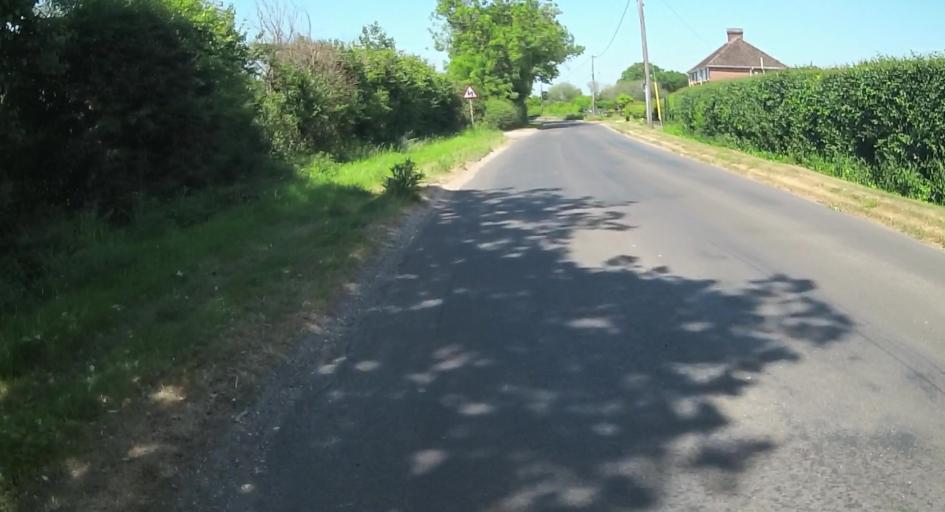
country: GB
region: England
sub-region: Hampshire
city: Tadley
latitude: 51.3195
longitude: -1.1693
